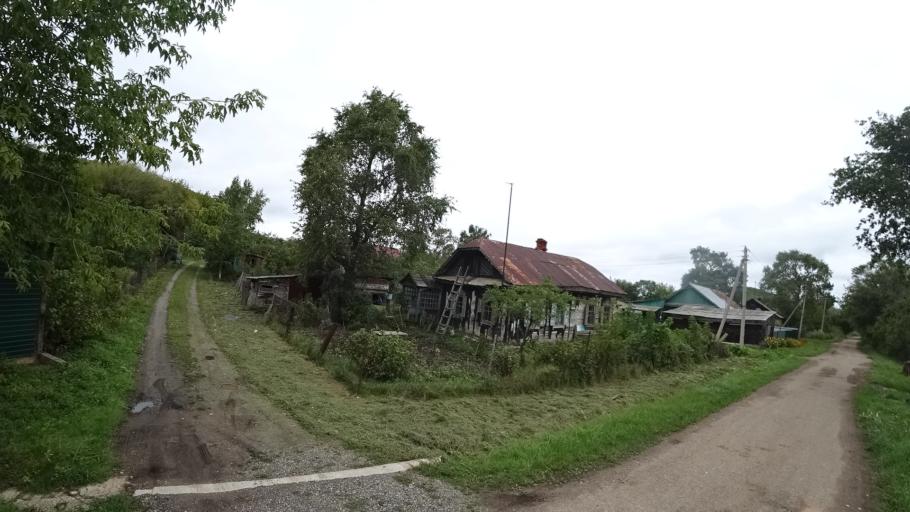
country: RU
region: Primorskiy
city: Chernigovka
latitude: 44.4601
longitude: 132.5889
